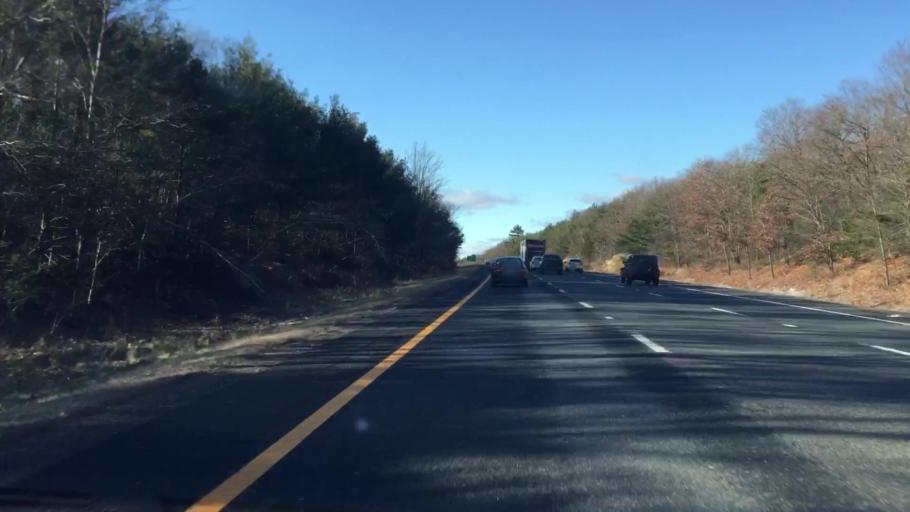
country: US
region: Massachusetts
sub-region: Norfolk County
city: Franklin
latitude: 42.0553
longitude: -71.3752
